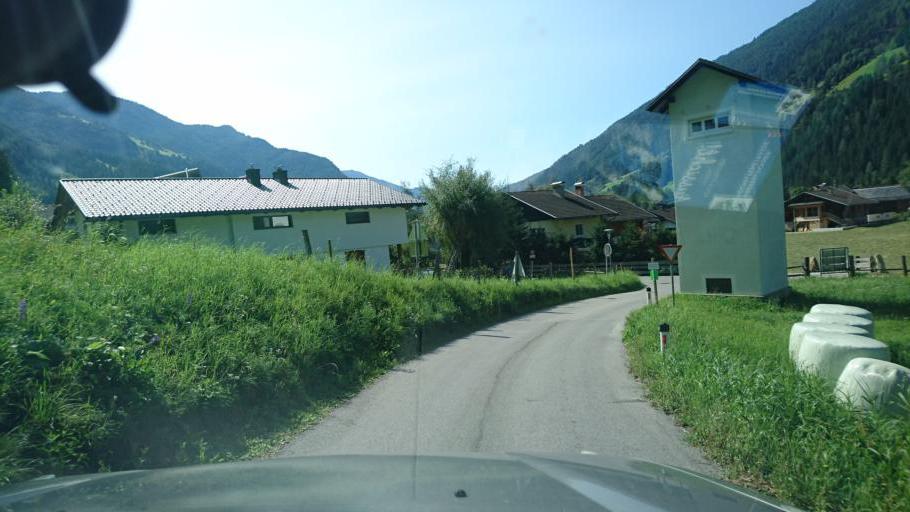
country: AT
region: Carinthia
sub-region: Politischer Bezirk Spittal an der Drau
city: Grosskirchheim
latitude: 46.9750
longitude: 12.8945
